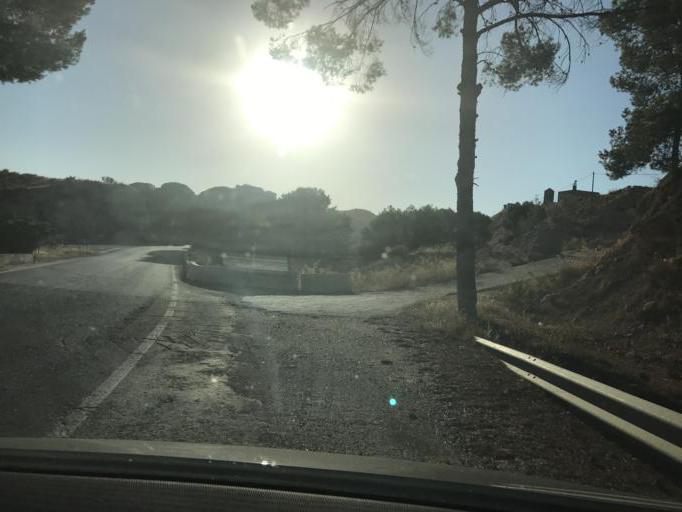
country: ES
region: Andalusia
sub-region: Provincia de Almeria
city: Bedar
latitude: 37.1392
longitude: -2.0184
